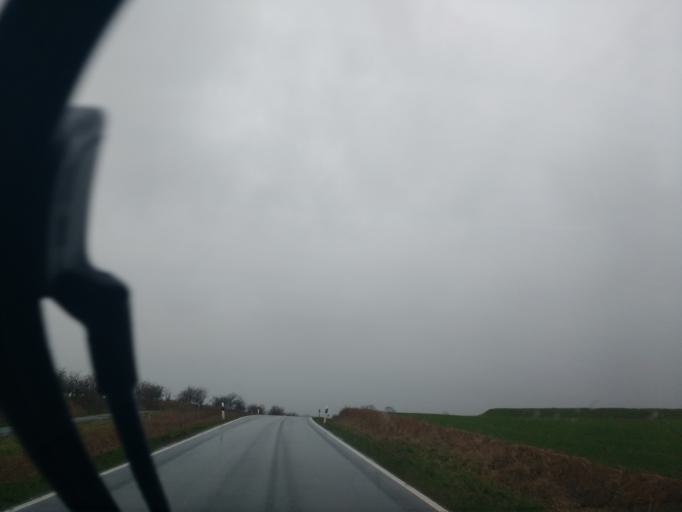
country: DE
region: Schleswig-Holstein
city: Oldenburg in Holstein
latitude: 54.3079
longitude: 10.9184
